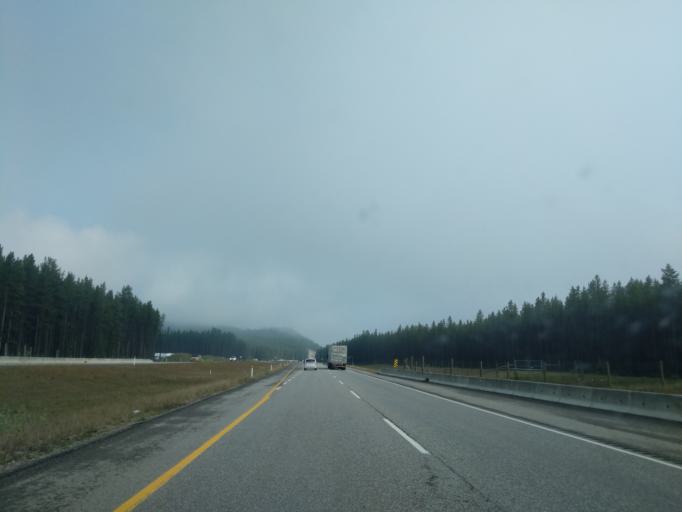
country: CA
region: Alberta
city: Lake Louise
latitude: 51.3038
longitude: -116.0171
